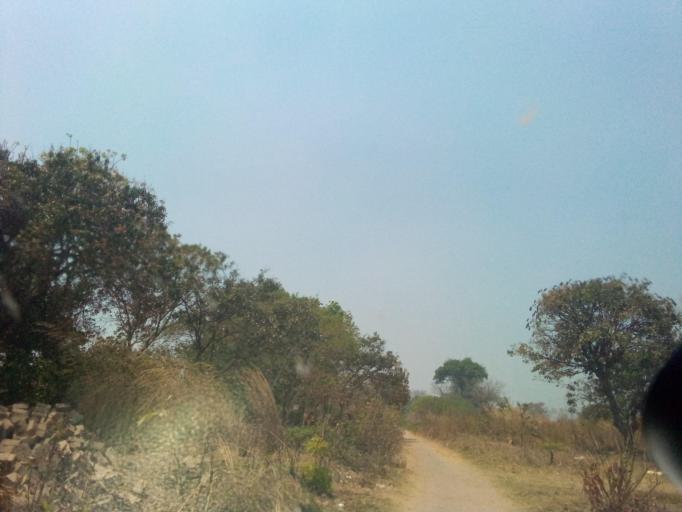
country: ZM
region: Copperbelt
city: Kataba
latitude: -12.2428
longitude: 30.3225
